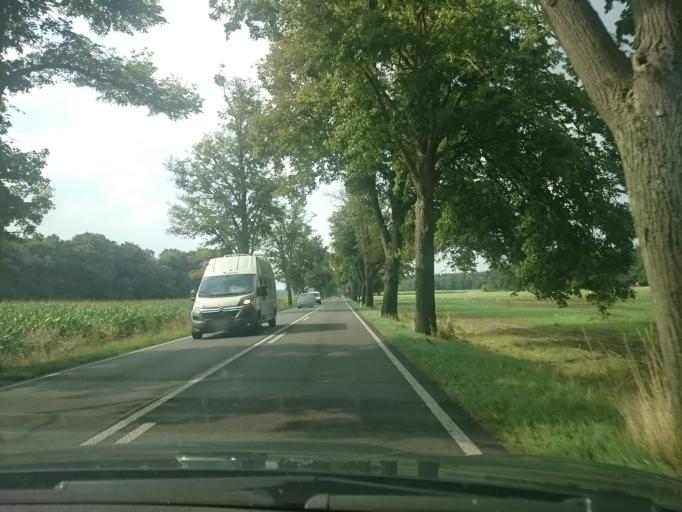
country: DE
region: Mecklenburg-Vorpommern
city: Ducherow
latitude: 53.7204
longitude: 13.8249
